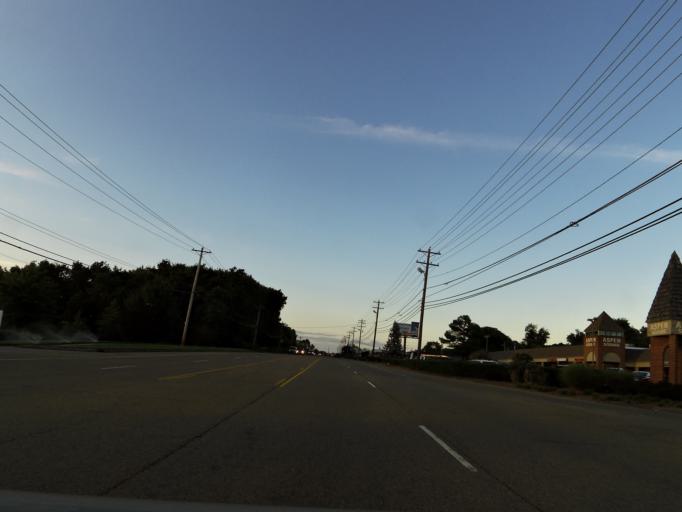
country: US
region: Tennessee
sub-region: Knox County
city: Farragut
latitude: 35.8872
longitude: -84.1498
